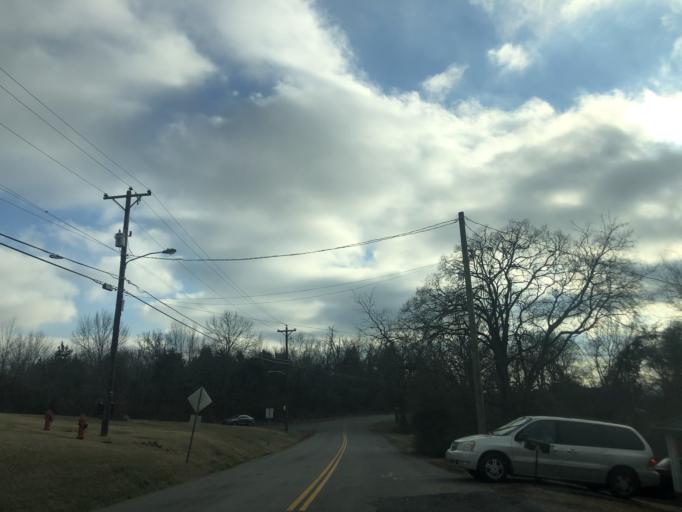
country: US
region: Tennessee
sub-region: Davidson County
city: Nashville
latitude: 36.2143
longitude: -86.7951
